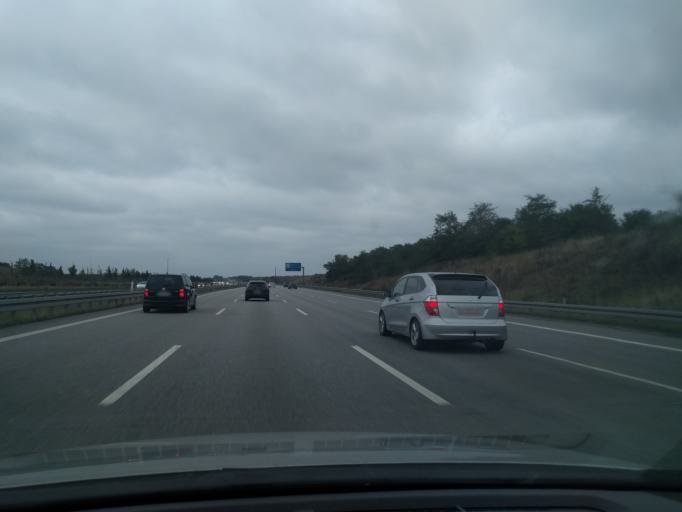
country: DK
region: Zealand
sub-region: Solrod Kommune
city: Solrod Strand
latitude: 55.5724
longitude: 12.2476
